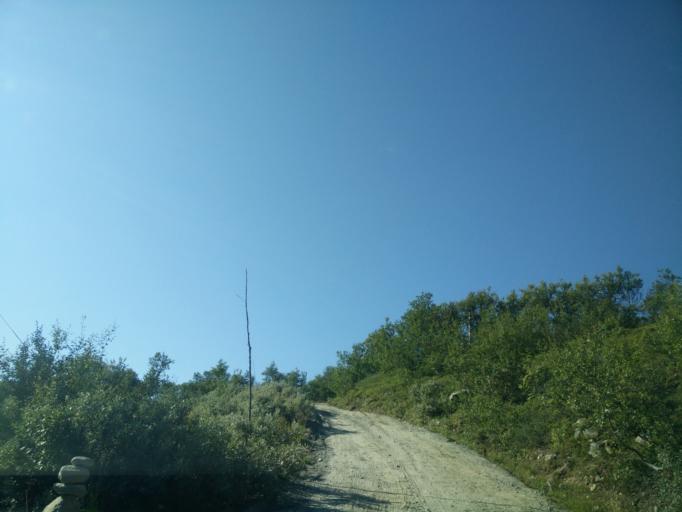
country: NO
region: Sor-Trondelag
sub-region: Tydal
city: Aas
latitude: 62.5750
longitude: 12.2008
